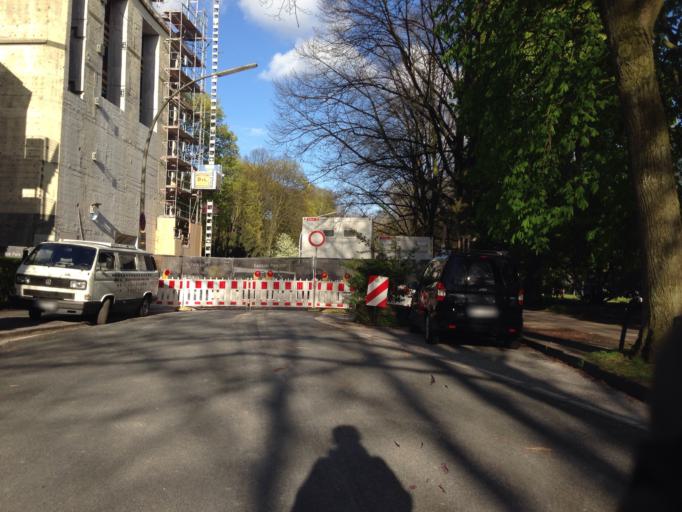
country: DE
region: Hamburg
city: Borgfelde
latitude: 53.5651
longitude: 10.0521
